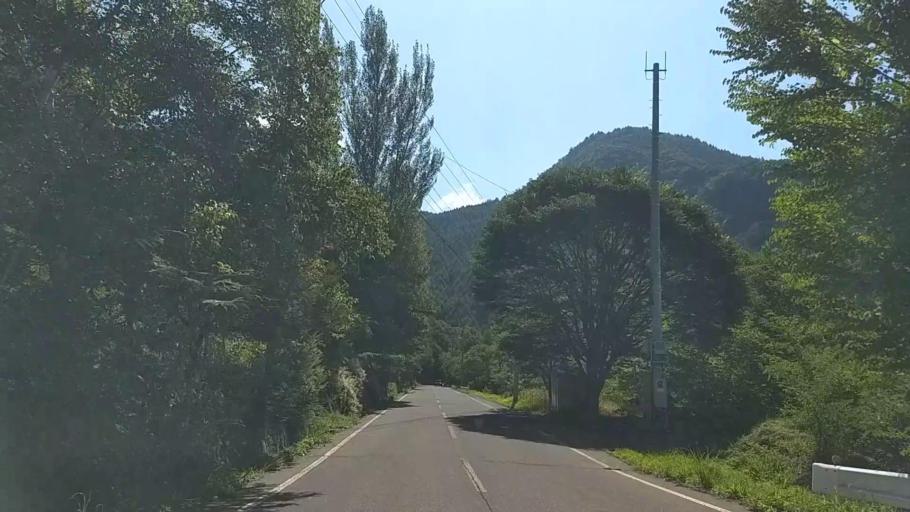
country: JP
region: Nagano
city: Matsumoto
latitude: 36.2074
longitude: 138.0935
